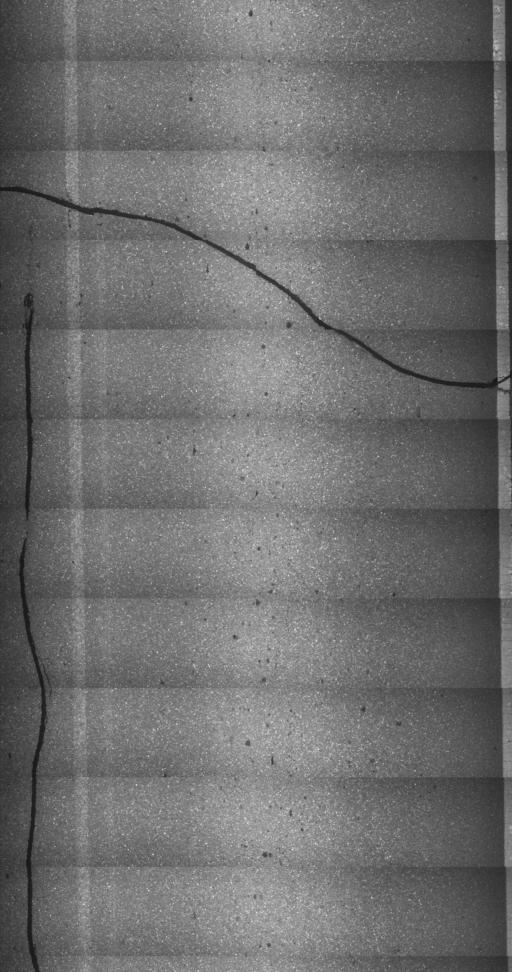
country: US
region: Vermont
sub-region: Orleans County
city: Newport
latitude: 44.7057
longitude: -72.1877
